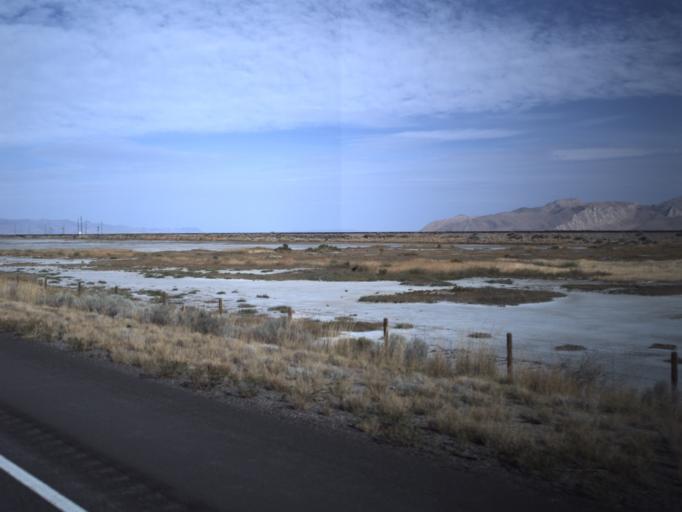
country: US
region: Utah
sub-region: Tooele County
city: Grantsville
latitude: 40.6822
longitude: -112.4285
